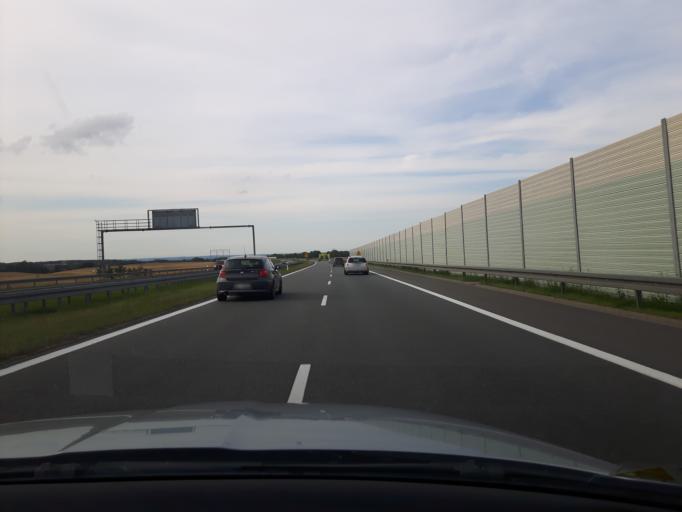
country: PL
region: Warmian-Masurian Voivodeship
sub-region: Powiat ostrodzki
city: Maldyty
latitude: 53.9814
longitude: 19.6966
